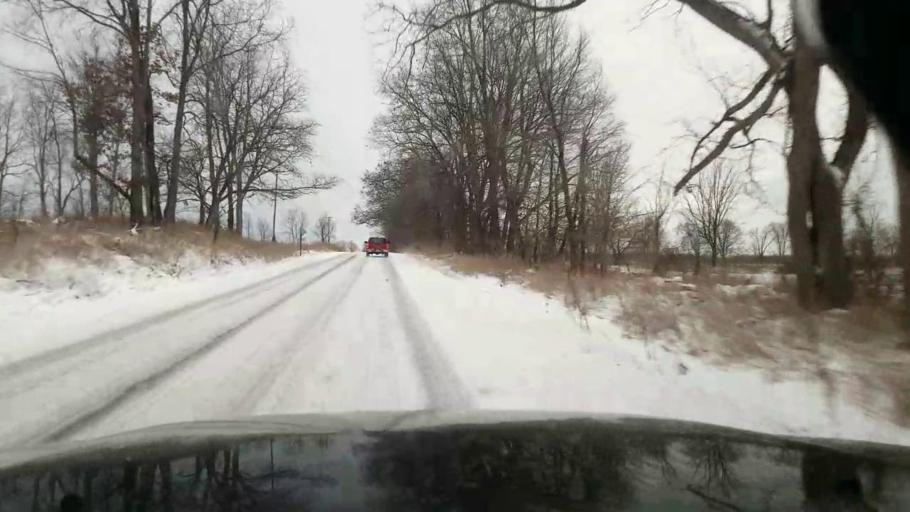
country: US
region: Michigan
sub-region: Jackson County
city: Spring Arbor
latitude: 42.1515
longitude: -84.4992
